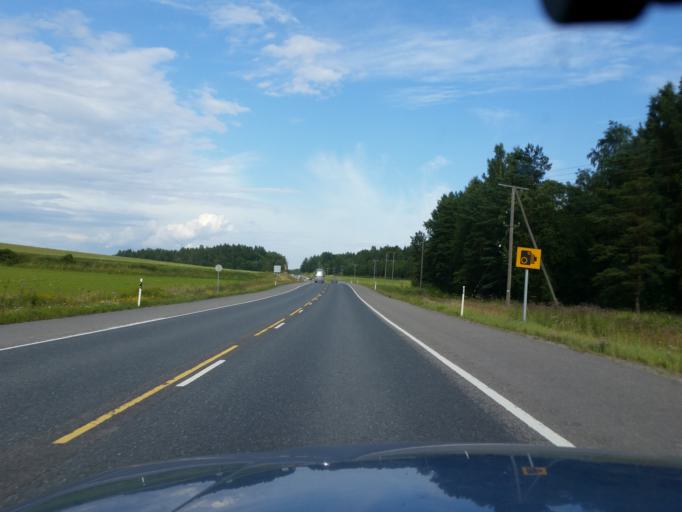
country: FI
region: Uusimaa
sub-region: Helsinki
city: Siuntio
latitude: 60.0834
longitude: 24.1855
